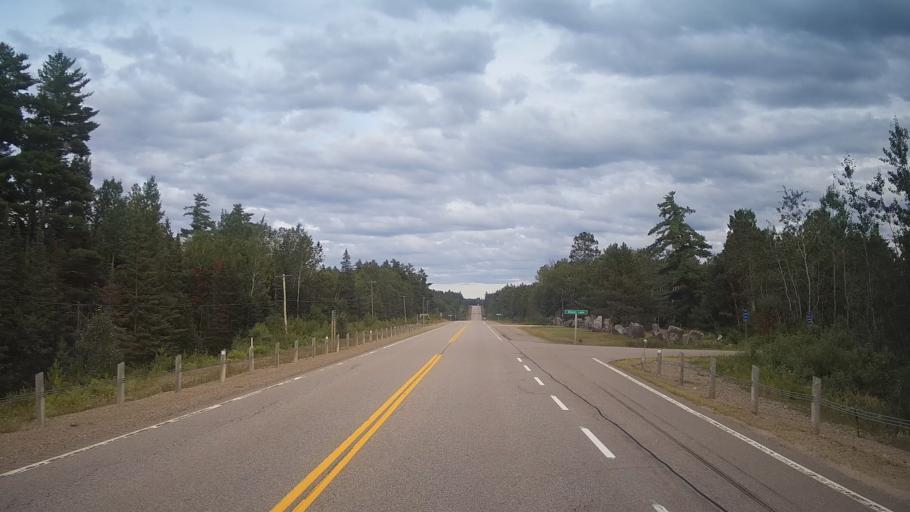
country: CA
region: Ontario
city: Mattawa
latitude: 46.2483
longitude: -78.1818
